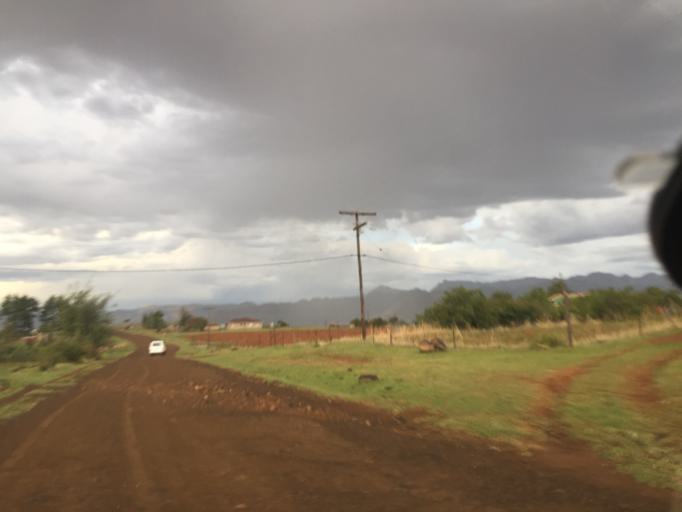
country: LS
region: Leribe
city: Leribe
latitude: -29.1541
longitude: 28.0380
